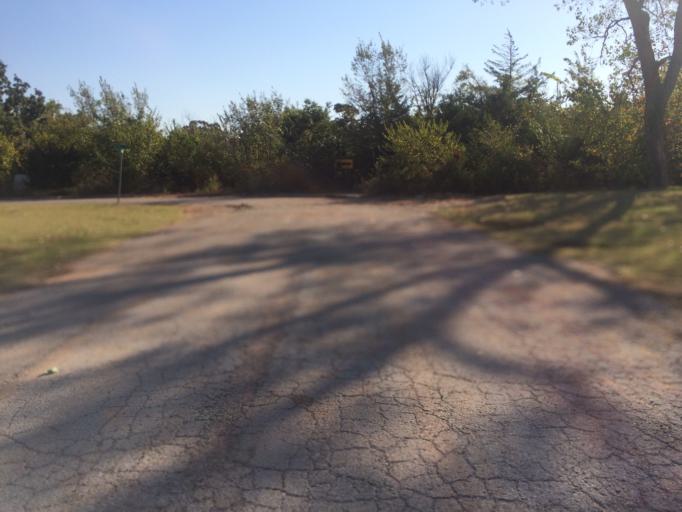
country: US
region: Oklahoma
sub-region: Cleveland County
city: Norman
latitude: 35.1809
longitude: -97.4326
